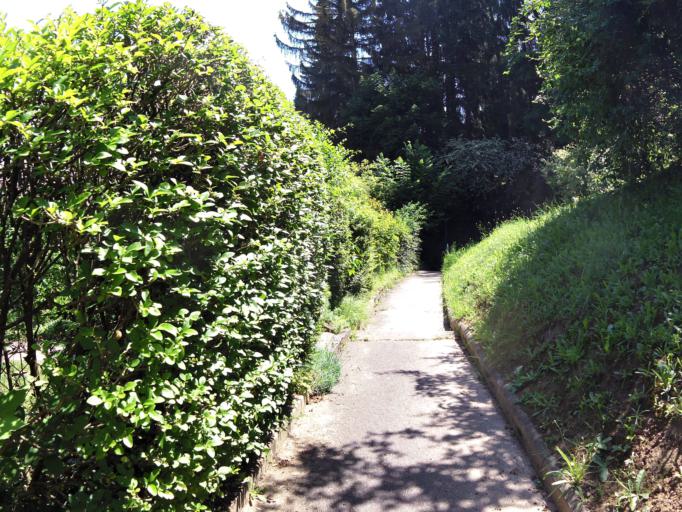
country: DE
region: Baden-Wuerttemberg
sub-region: Freiburg Region
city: Lahr
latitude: 48.3318
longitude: 7.8594
